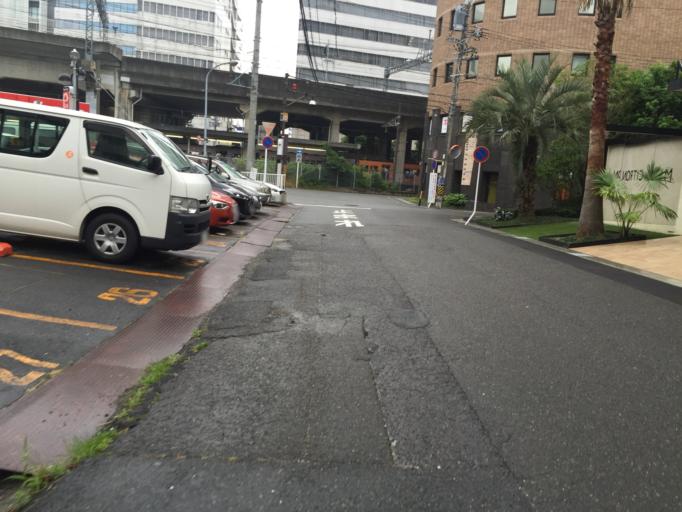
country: JP
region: Mie
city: Yokkaichi
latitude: 34.9657
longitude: 136.6176
